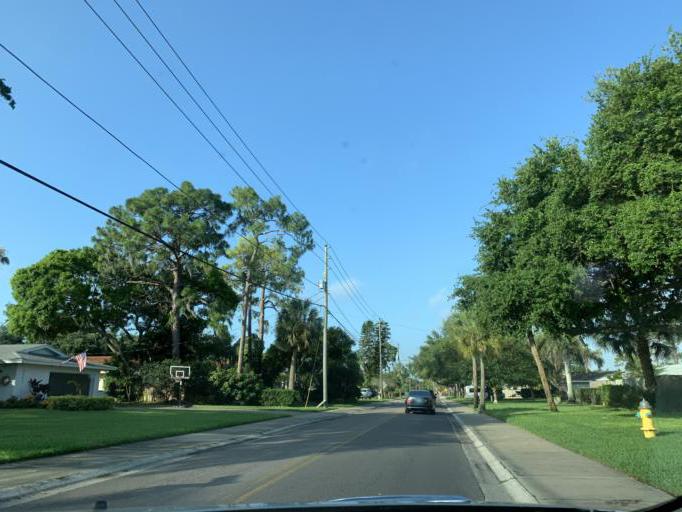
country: US
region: Florida
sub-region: Pinellas County
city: Gandy
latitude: 27.8173
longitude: -82.6072
